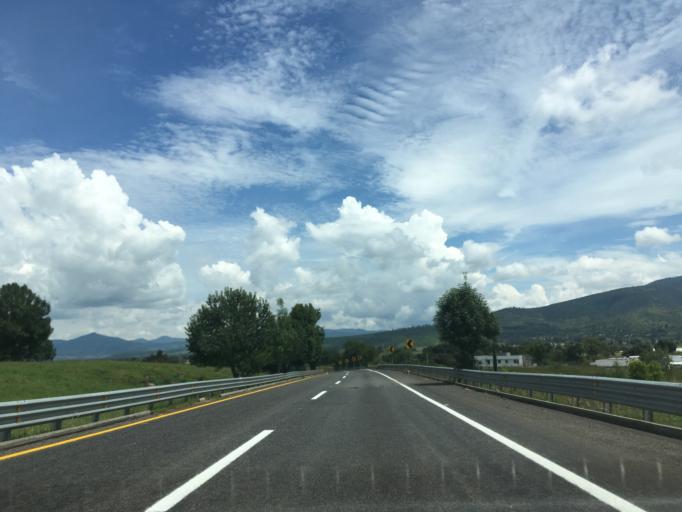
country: MX
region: Michoacan
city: Acuitzio del Canje
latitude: 19.5558
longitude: -101.3383
